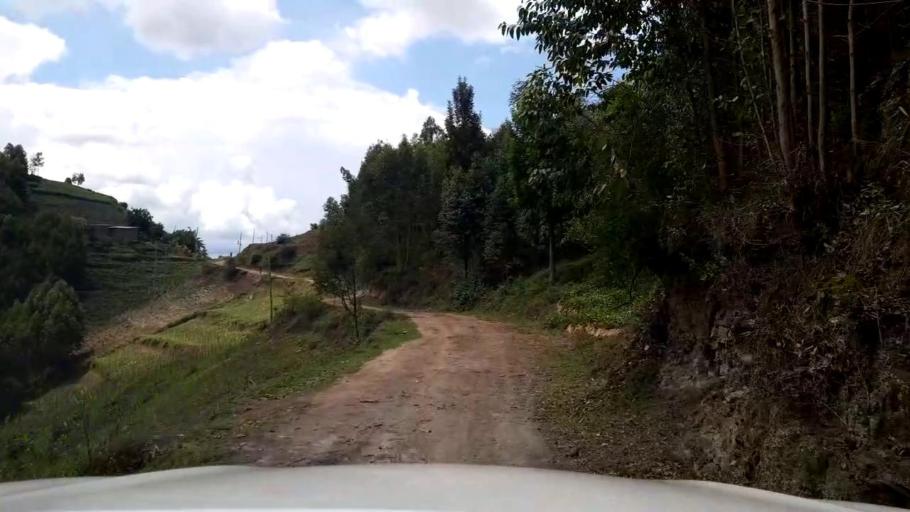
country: RW
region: Northern Province
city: Byumba
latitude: -1.5201
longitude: 30.1285
